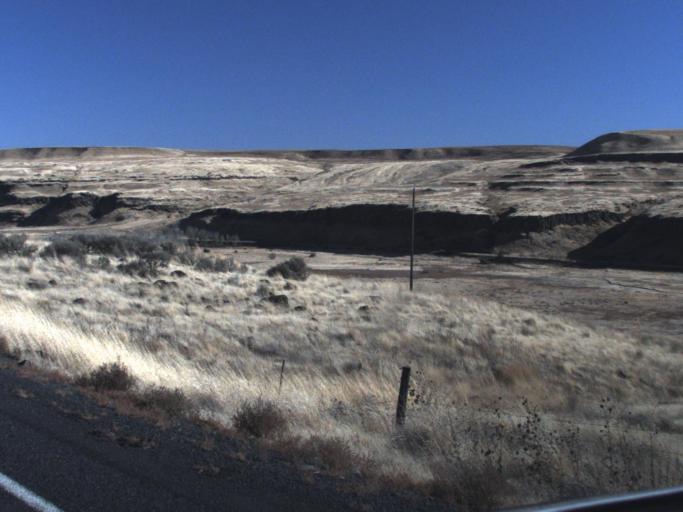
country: US
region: Washington
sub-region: Franklin County
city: Connell
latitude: 46.6509
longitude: -118.5216
